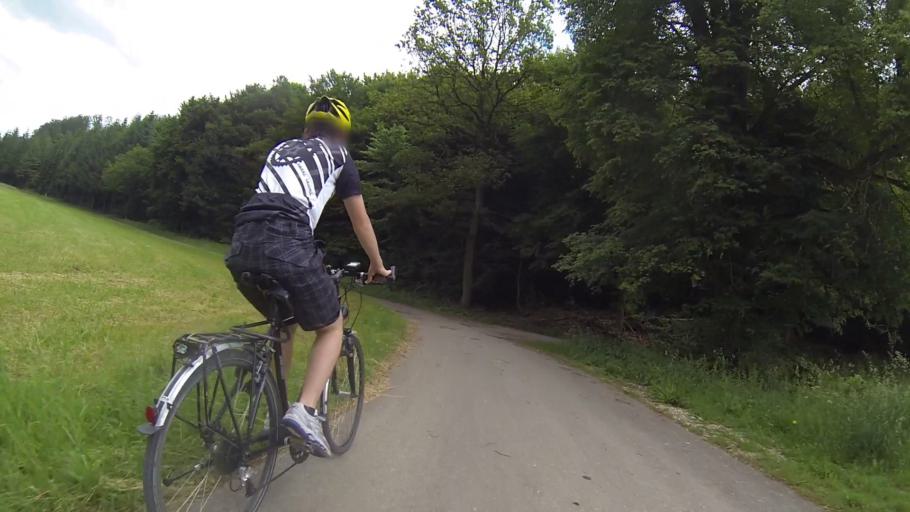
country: DE
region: Baden-Wuerttemberg
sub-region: Regierungsbezirk Stuttgart
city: Gerstetten
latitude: 48.6674
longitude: 10.0368
